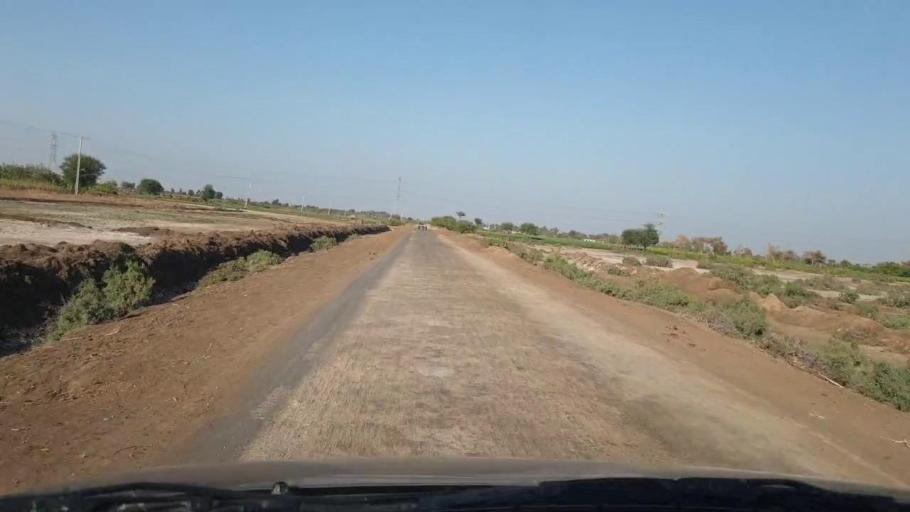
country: PK
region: Sindh
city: Samaro
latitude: 25.1470
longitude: 69.3072
